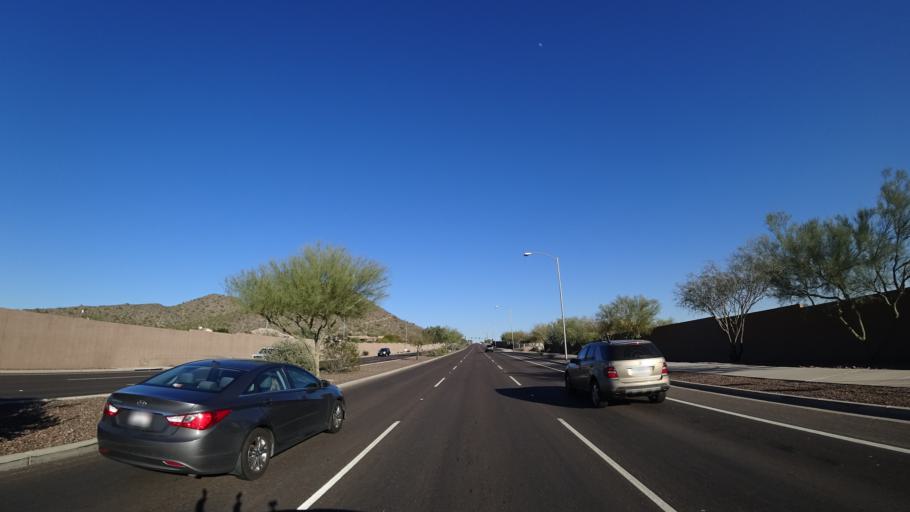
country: US
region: Arizona
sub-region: Maricopa County
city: Sun City West
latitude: 33.7106
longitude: -112.2585
